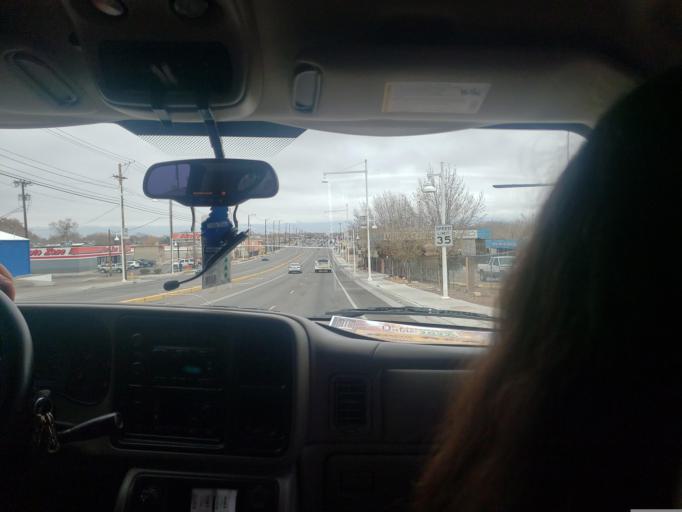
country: US
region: New Mexico
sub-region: Bernalillo County
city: Albuquerque
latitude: 35.0837
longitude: -106.6946
